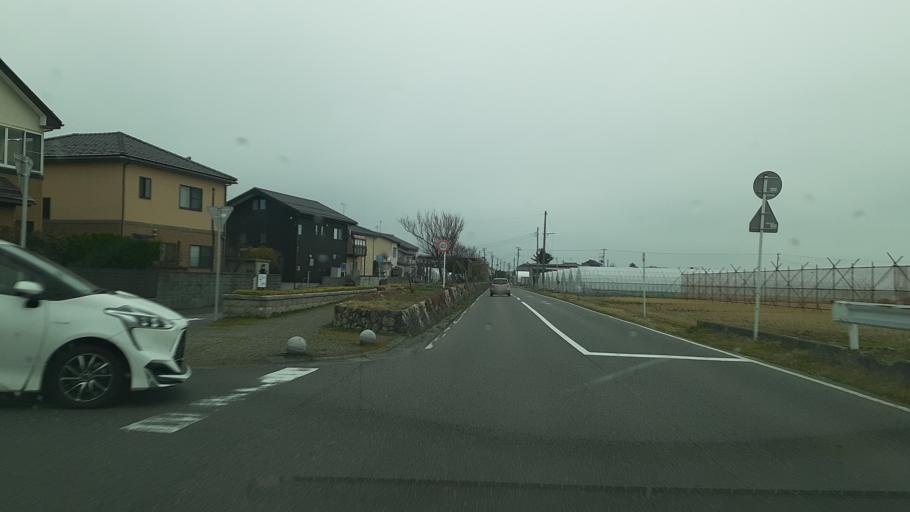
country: JP
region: Niigata
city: Niigata-shi
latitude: 37.8630
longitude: 139.0369
